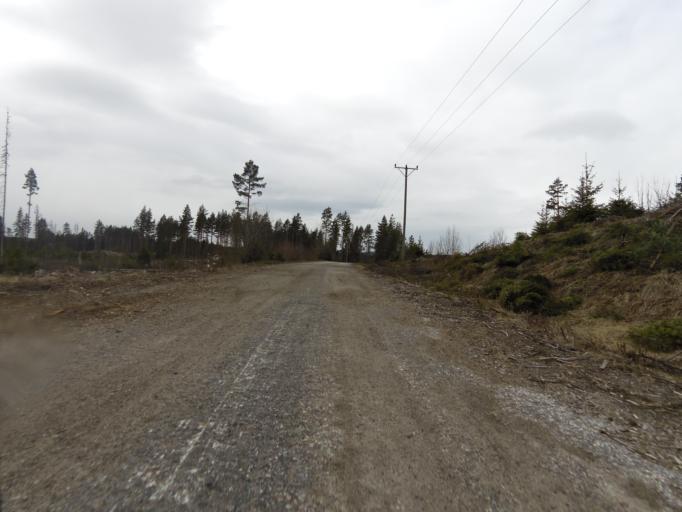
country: SE
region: Gaevleborg
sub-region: Hofors Kommun
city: Hofors
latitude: 60.5407
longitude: 16.2122
